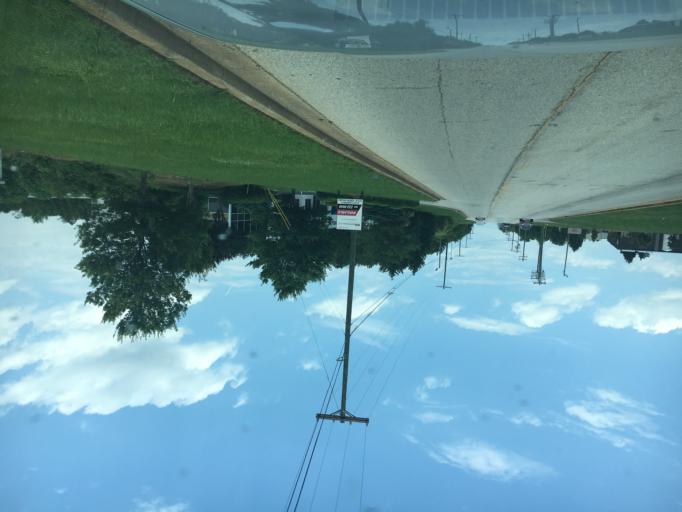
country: US
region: South Carolina
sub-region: Greenville County
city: Five Forks
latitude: 34.8717
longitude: -82.2300
